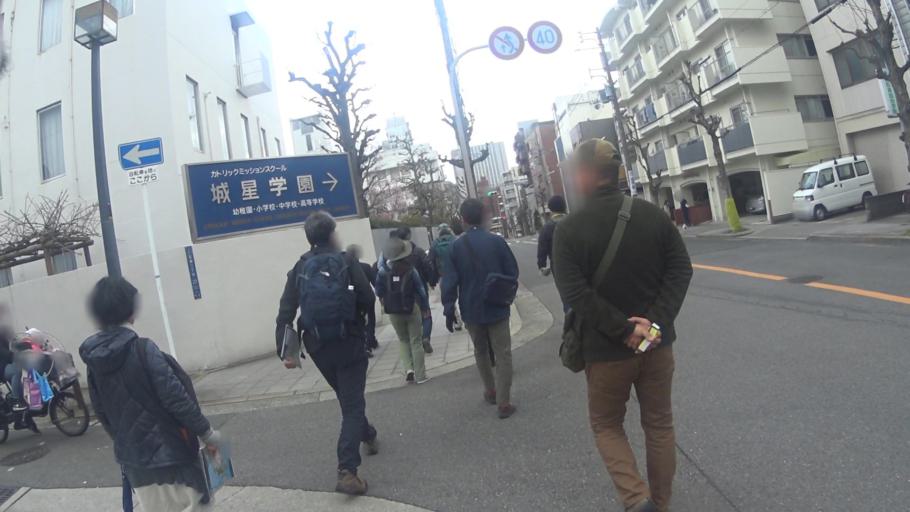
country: JP
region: Osaka
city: Osaka-shi
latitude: 34.6779
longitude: 135.5275
